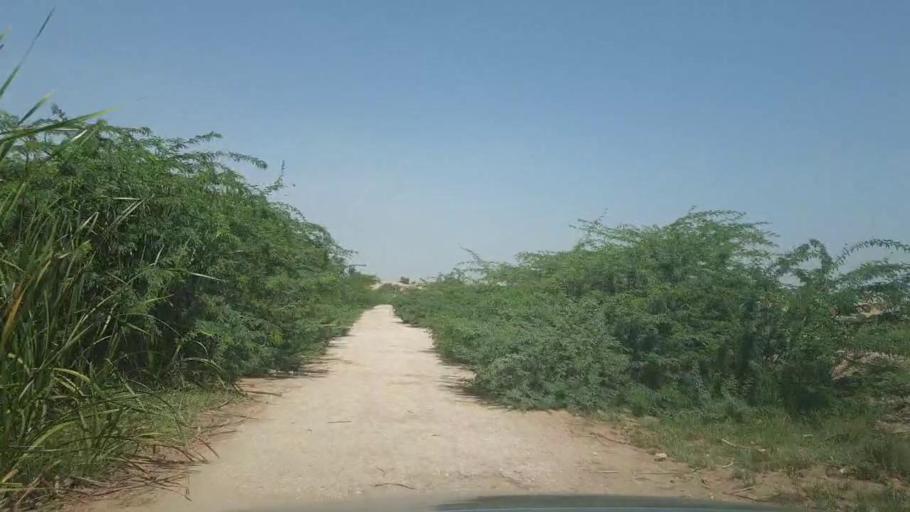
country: PK
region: Sindh
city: Kot Diji
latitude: 27.3239
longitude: 69.0157
